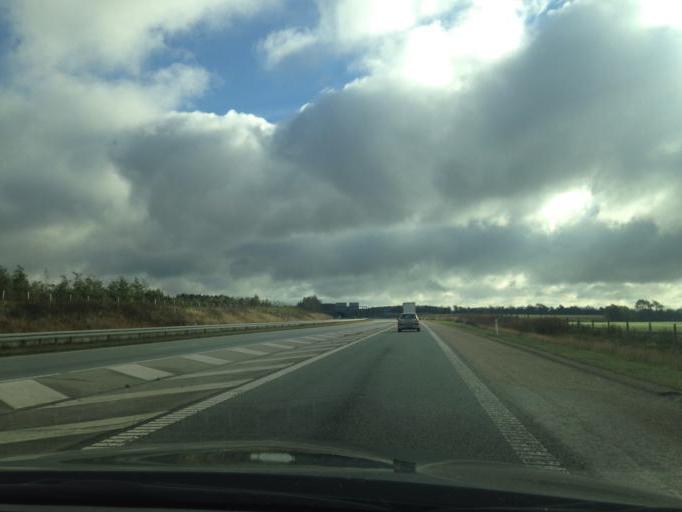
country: DK
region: South Denmark
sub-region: Vejle Kommune
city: Give
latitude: 55.8405
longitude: 9.2788
